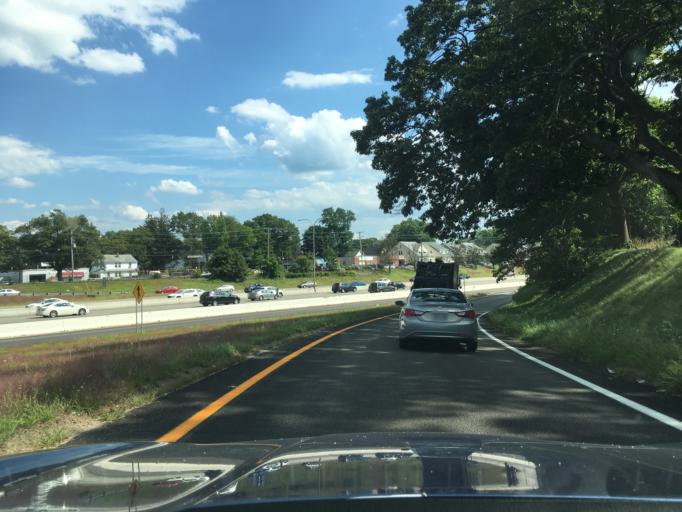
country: US
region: Rhode Island
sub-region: Providence County
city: Cranston
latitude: 41.7807
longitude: -71.4259
